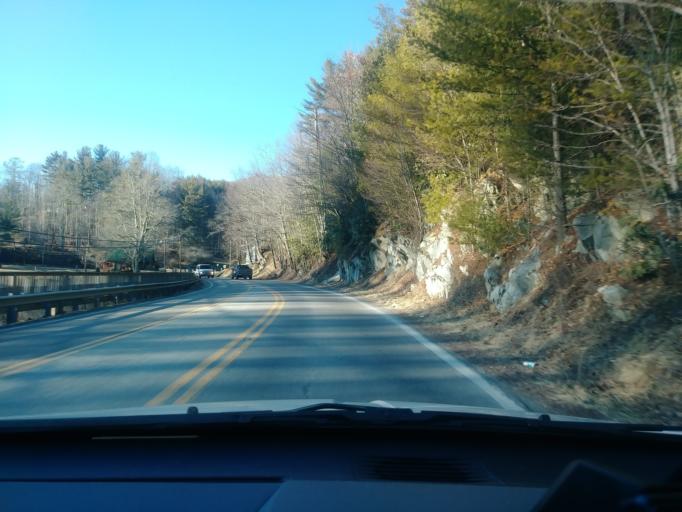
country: US
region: North Carolina
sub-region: Avery County
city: Banner Elk
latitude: 36.1571
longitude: -81.8696
